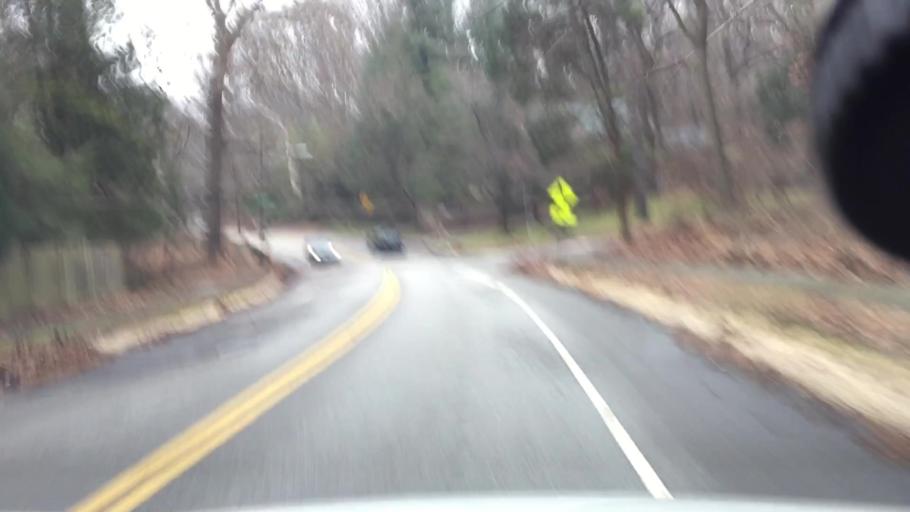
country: US
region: Pennsylvania
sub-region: Montgomery County
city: Wyndmoor
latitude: 40.0580
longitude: -75.2000
